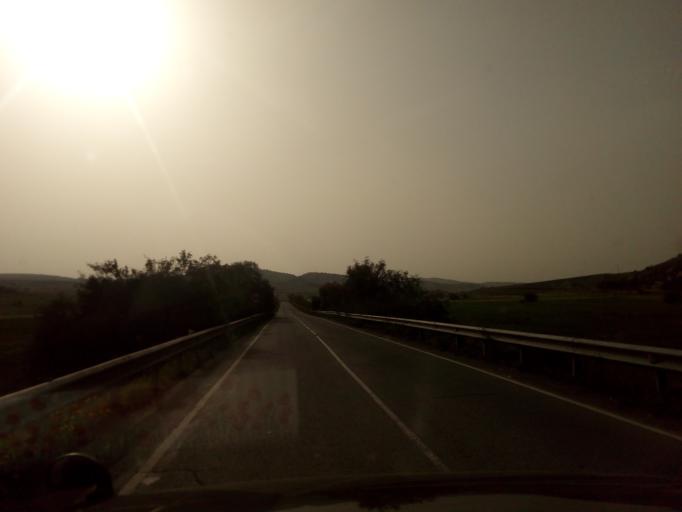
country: CY
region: Lefkosia
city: Lympia
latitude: 35.0023
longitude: 33.4990
